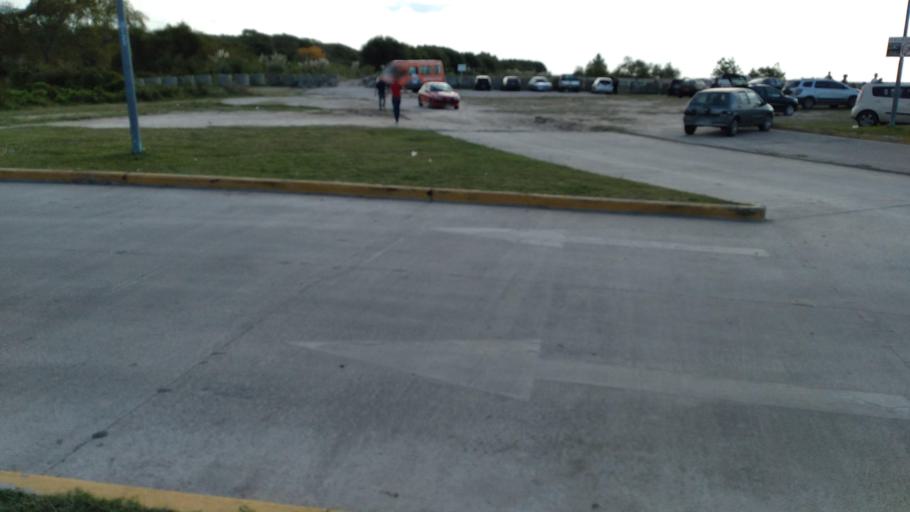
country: AR
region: Buenos Aires
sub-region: Partido de Quilmes
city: Quilmes
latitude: -34.7535
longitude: -58.1094
